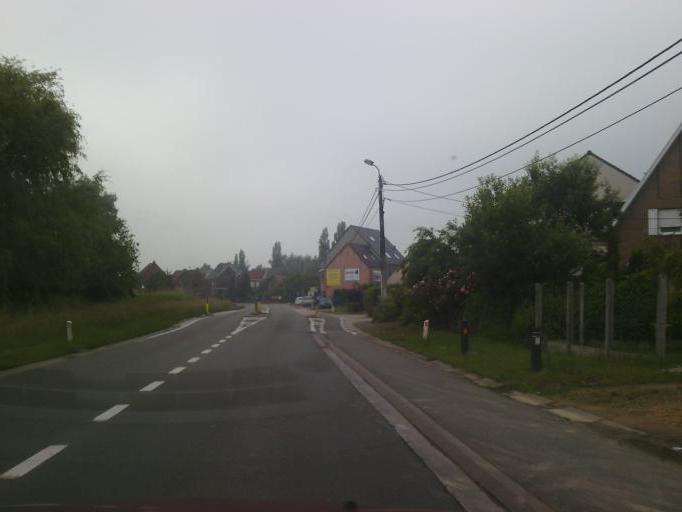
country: BE
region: Flanders
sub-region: Provincie Oost-Vlaanderen
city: Aalst
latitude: 50.9902
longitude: 4.0515
